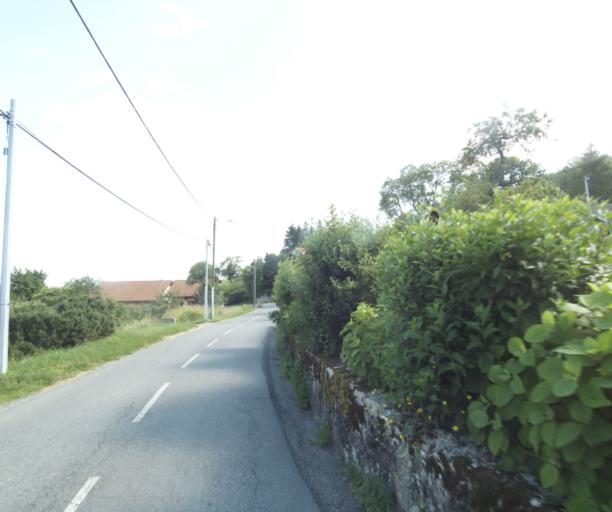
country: FR
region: Rhone-Alpes
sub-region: Departement de la Haute-Savoie
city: Lyaud
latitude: 46.3168
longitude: 6.5103
